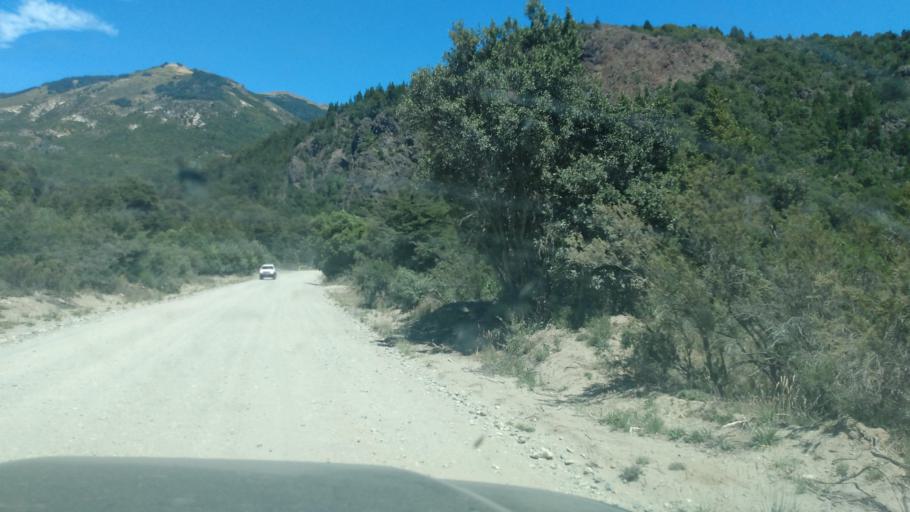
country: AR
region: Rio Negro
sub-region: Departamento de Bariloche
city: San Carlos de Bariloche
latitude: -41.1285
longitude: -71.4503
